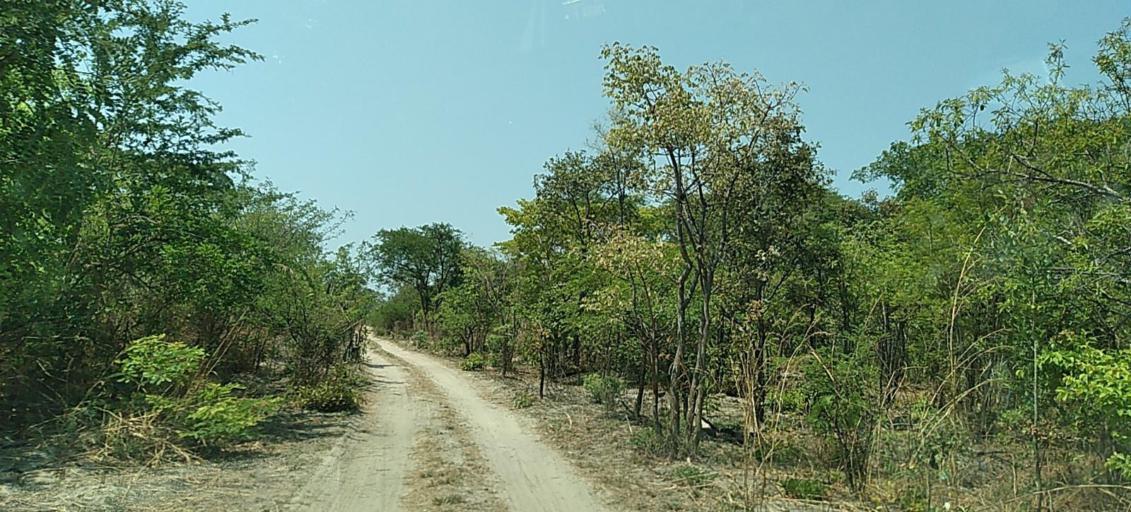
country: ZM
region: Copperbelt
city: Mpongwe
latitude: -13.8379
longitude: 28.0595
